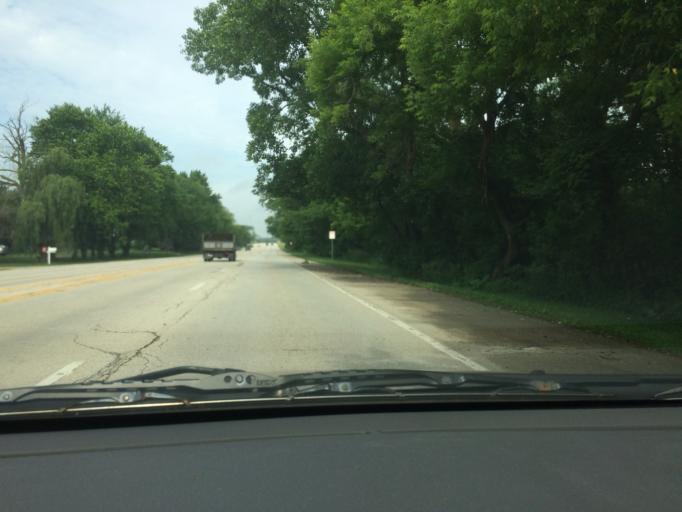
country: US
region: Illinois
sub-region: Cook County
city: Bartlett
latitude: 41.9440
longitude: -88.1850
